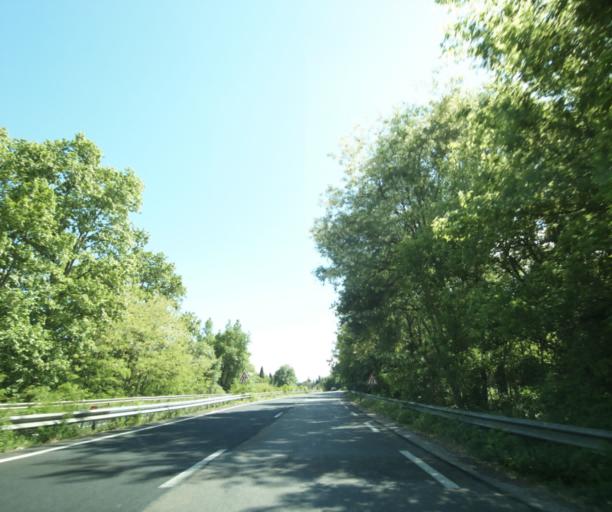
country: FR
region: Languedoc-Roussillon
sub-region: Departement de l'Herault
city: Laverune
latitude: 43.5980
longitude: 3.8200
